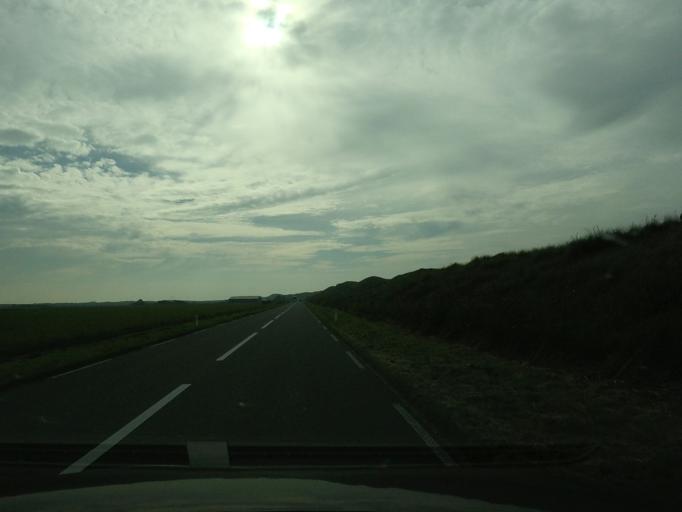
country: NL
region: North Holland
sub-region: Gemeente Den Helder
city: Den Helder
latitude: 52.8603
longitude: 4.7058
